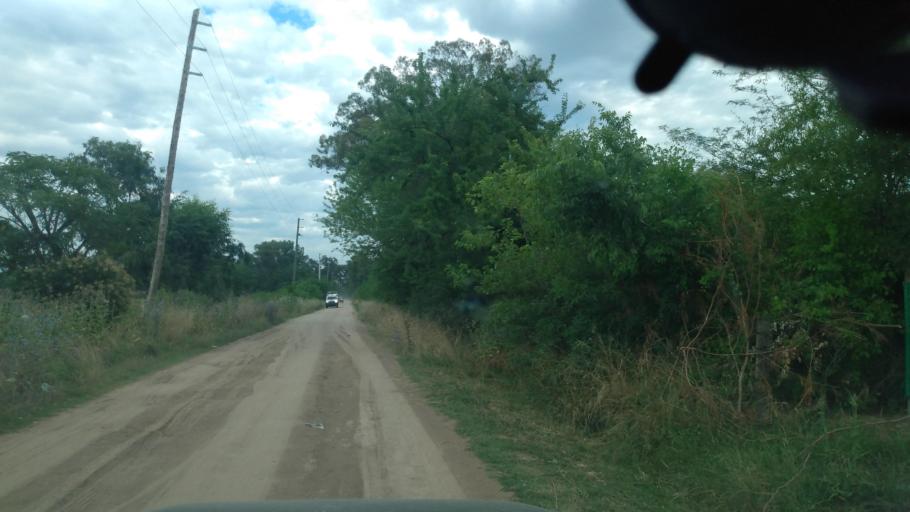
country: AR
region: Buenos Aires
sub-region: Partido de Lujan
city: Lujan
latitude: -34.5965
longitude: -59.0552
